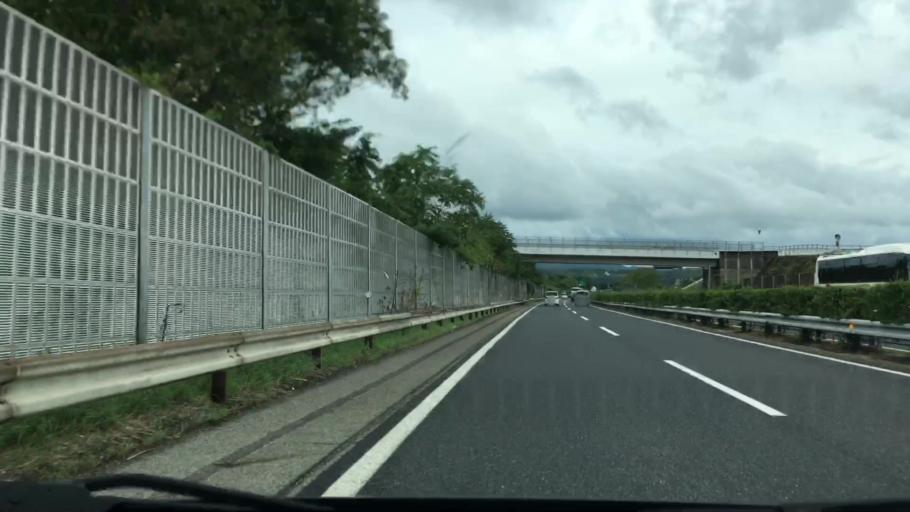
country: JP
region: Okayama
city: Tsuyama
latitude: 35.0225
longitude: 134.1811
